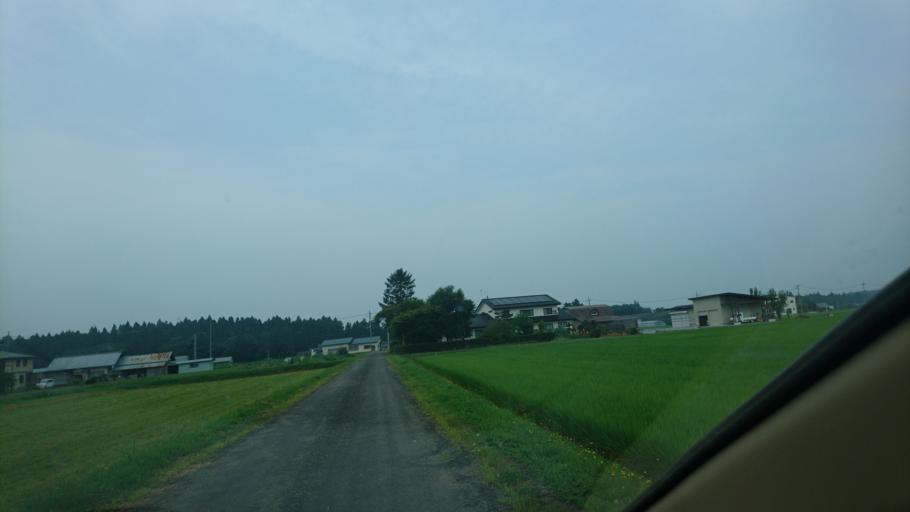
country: JP
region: Iwate
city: Kitakami
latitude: 39.2468
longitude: 141.0851
